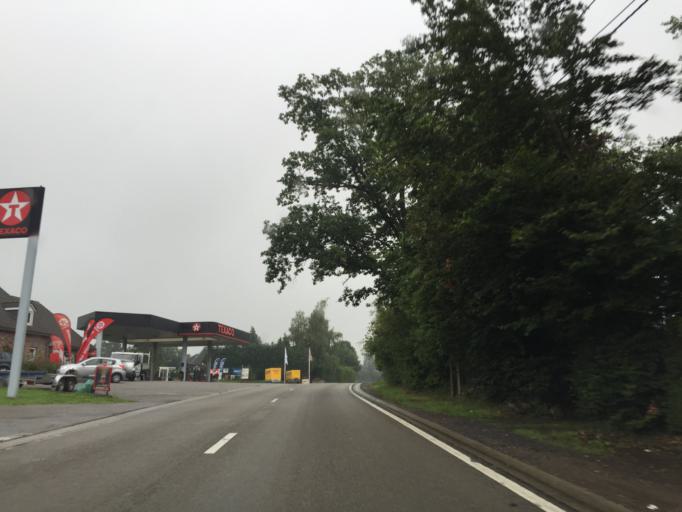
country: BE
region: Wallonia
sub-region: Province de Liege
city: Spa
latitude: 50.5146
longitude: 5.9081
